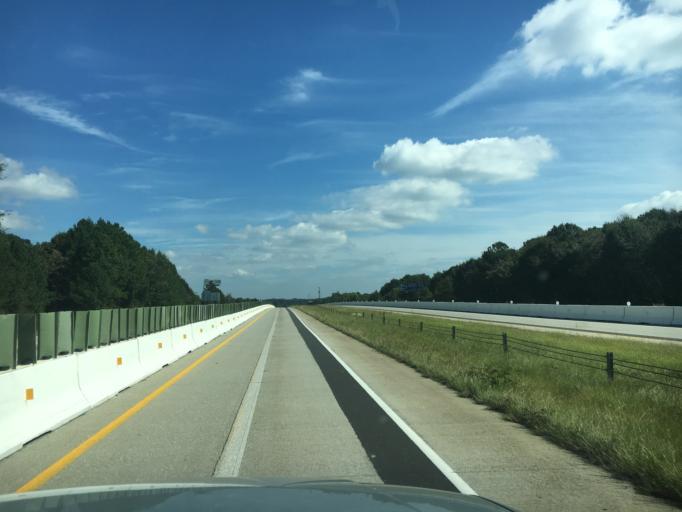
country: US
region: South Carolina
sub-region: Spartanburg County
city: Southern Shops
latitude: 35.0016
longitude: -81.9881
